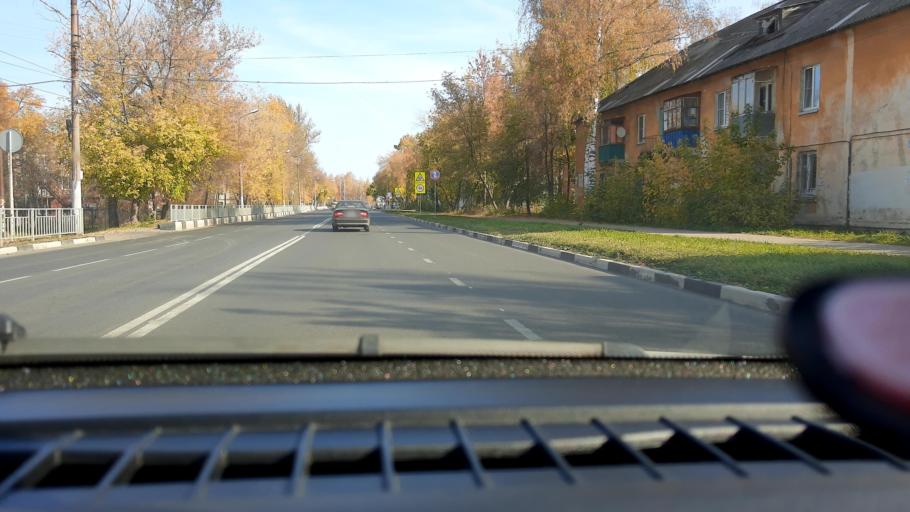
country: RU
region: Nizjnij Novgorod
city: Kstovo
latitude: 56.1546
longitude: 44.1938
